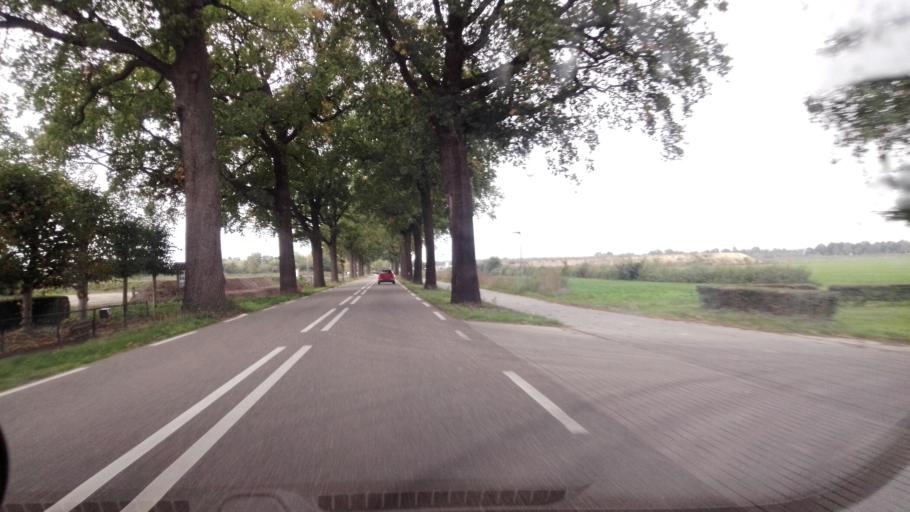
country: NL
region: Limburg
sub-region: Gemeente Peel en Maas
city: Maasbree
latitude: 51.4304
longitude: 6.0945
